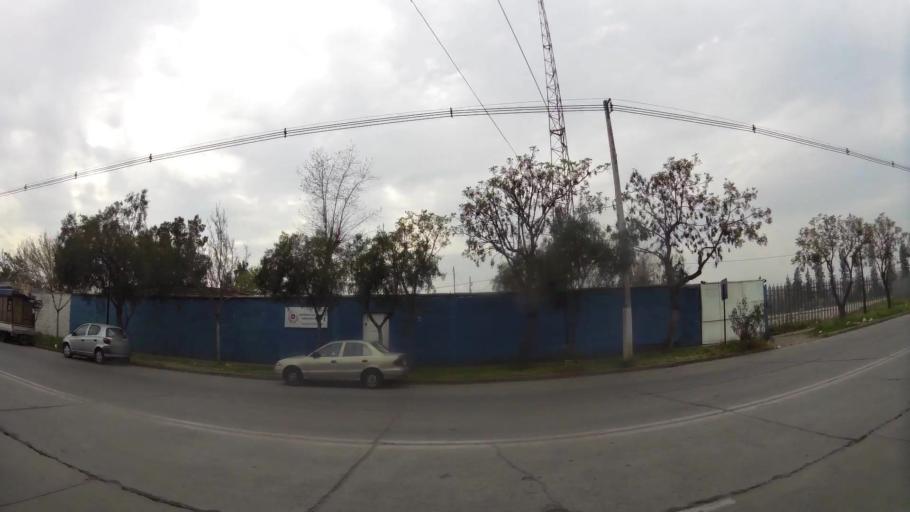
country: CL
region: Santiago Metropolitan
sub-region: Provincia de Santiago
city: Villa Presidente Frei, Nunoa, Santiago, Chile
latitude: -33.4707
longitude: -70.6123
